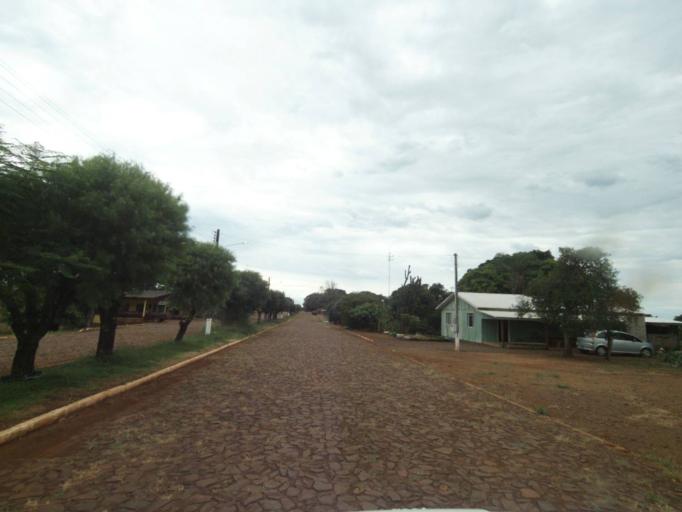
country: BR
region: Parana
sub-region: Guaraniacu
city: Guaraniacu
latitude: -24.9197
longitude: -52.9382
